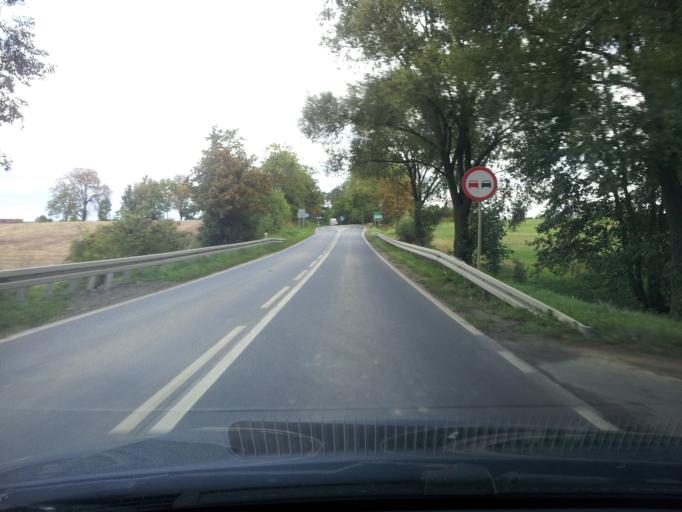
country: PL
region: Kujawsko-Pomorskie
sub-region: Powiat brodnicki
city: Brodnica
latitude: 53.1626
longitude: 19.3878
